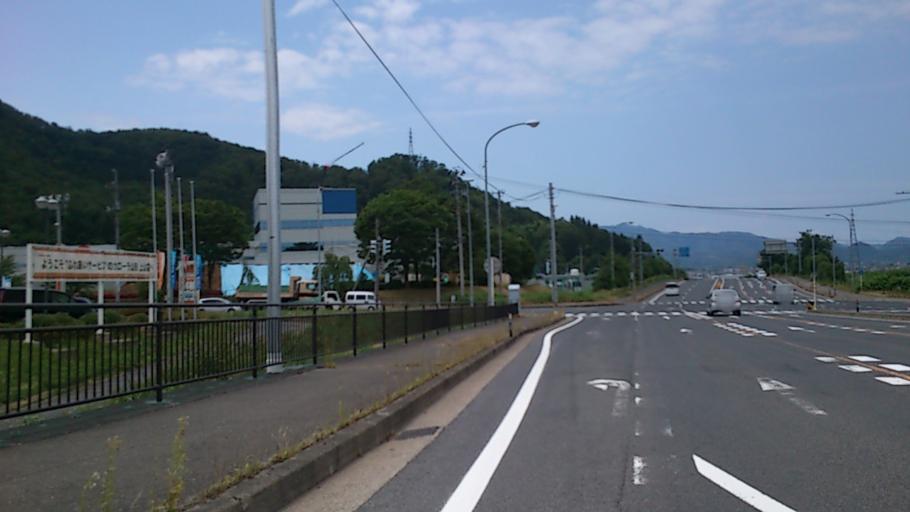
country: JP
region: Yamagata
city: Kaminoyama
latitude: 38.1643
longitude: 140.3050
